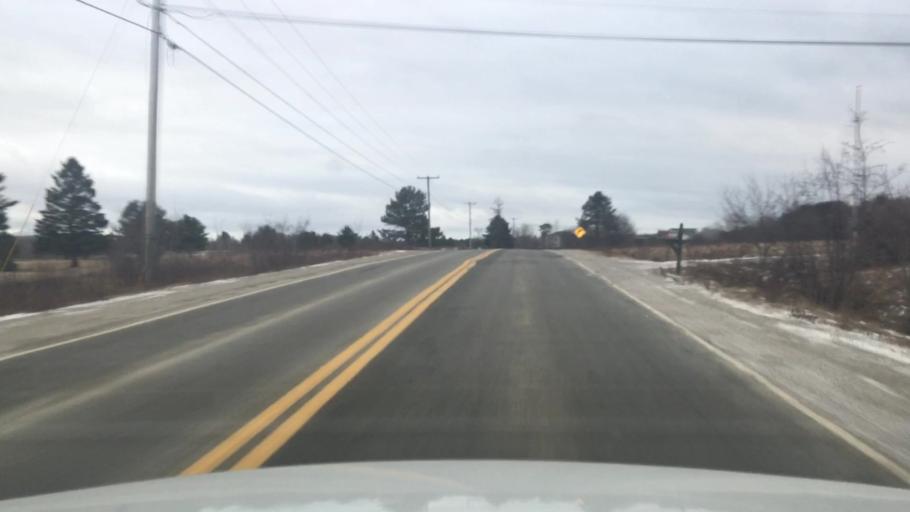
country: US
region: Maine
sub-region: Hancock County
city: Trenton
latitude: 44.4935
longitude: -68.3631
